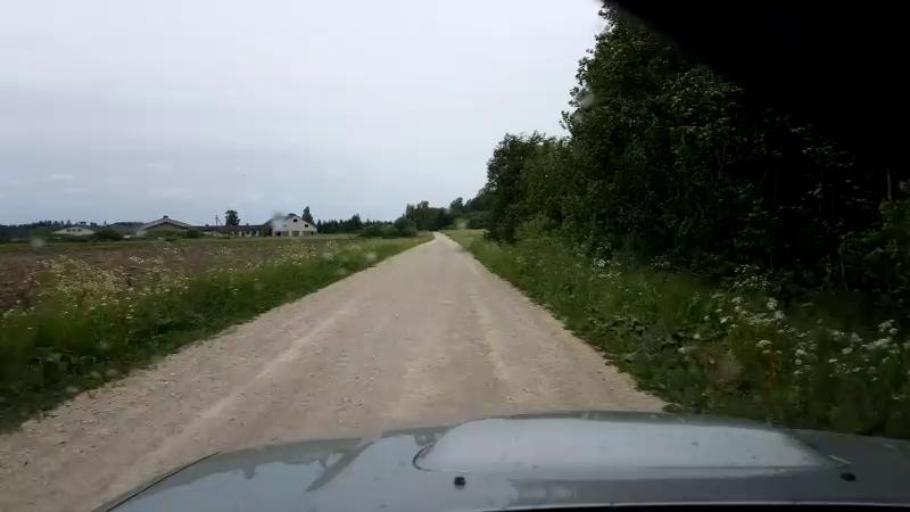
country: EE
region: Paernumaa
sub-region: Halinga vald
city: Parnu-Jaagupi
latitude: 58.5335
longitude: 24.5905
